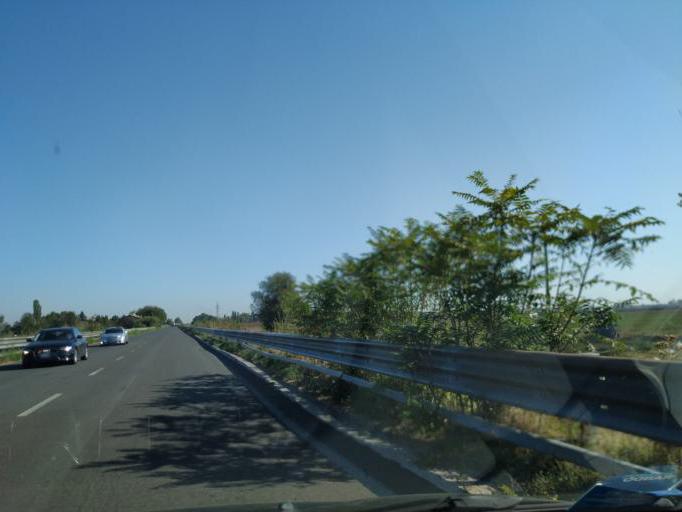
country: IT
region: Emilia-Romagna
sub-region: Provincia di Bologna
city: San Giovanni in Persiceto
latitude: 44.6677
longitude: 11.1881
